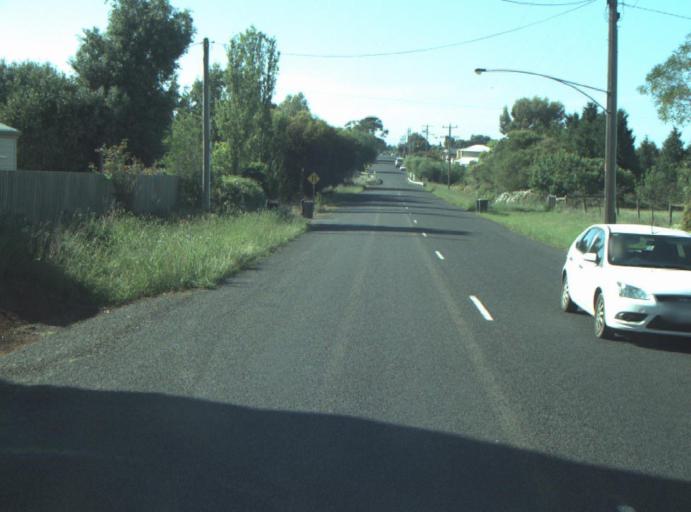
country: AU
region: Victoria
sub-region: Greater Geelong
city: Lara
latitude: -38.0130
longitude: 144.4015
